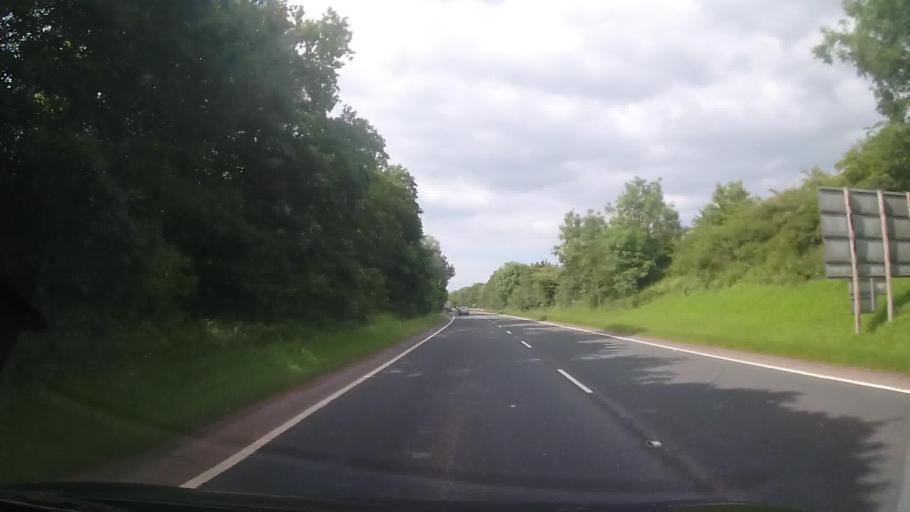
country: GB
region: England
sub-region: Shropshire
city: Ludlow
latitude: 52.3661
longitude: -2.6947
